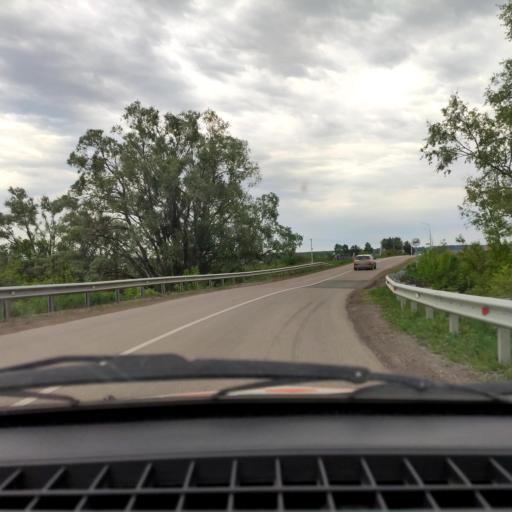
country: RU
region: Bashkortostan
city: Avdon
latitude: 54.5585
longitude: 55.7636
